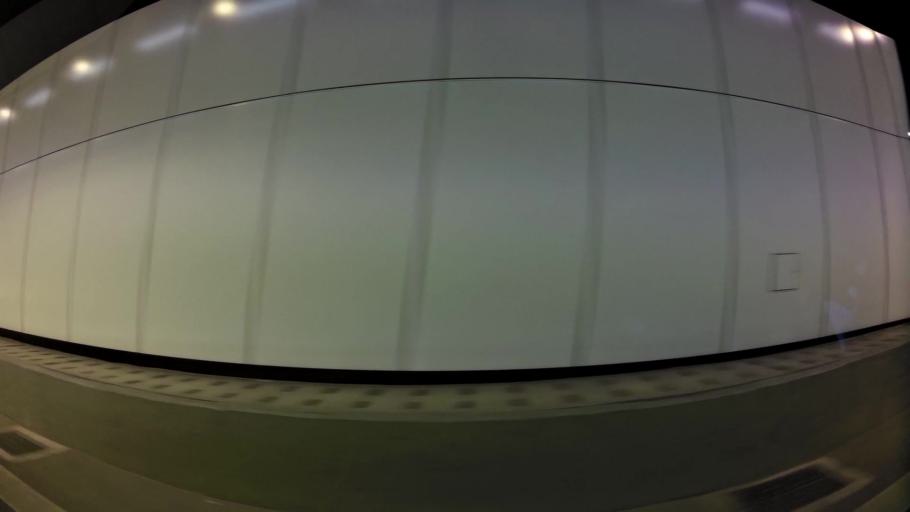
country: SG
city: Singapore
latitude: 1.3205
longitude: 103.8761
